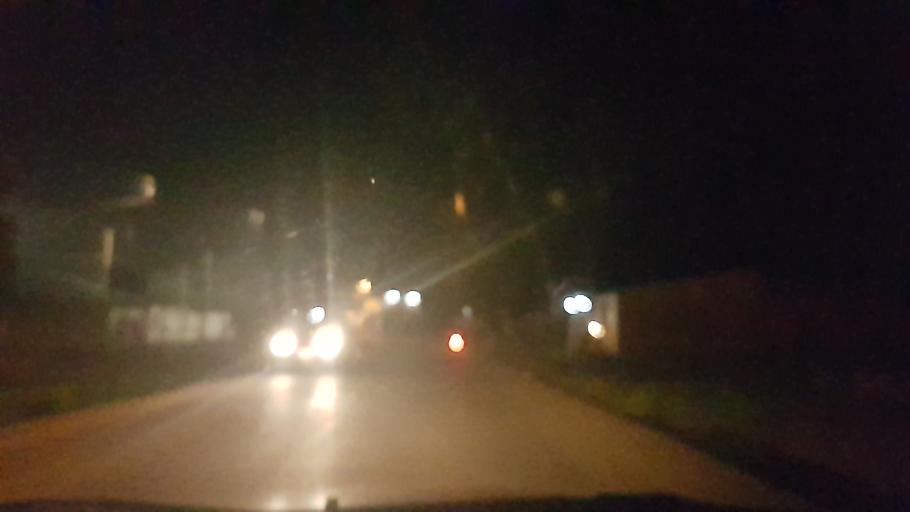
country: PY
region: Central
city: Colonia Mariano Roque Alonso
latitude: -25.1935
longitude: -57.5343
